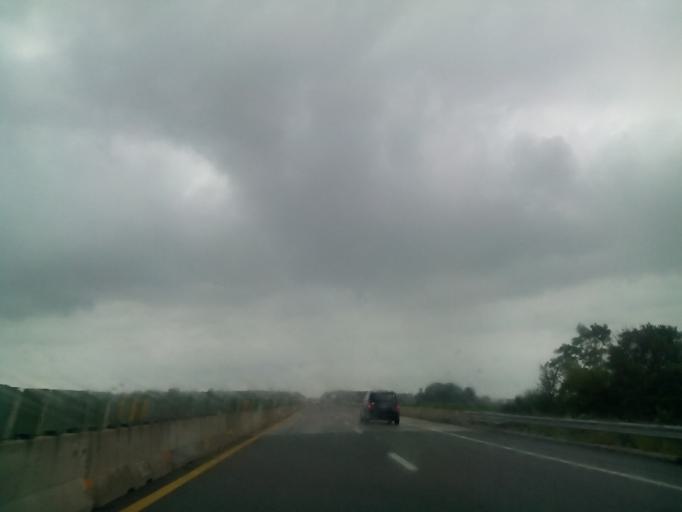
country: US
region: Ohio
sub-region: Sandusky County
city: Clyde
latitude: 41.3619
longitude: -82.9321
